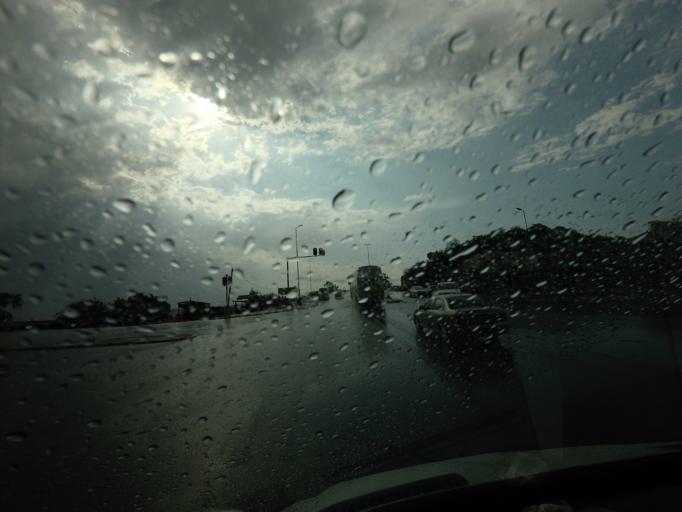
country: SZ
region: Manzini
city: Manzini
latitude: -26.4960
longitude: 31.3556
